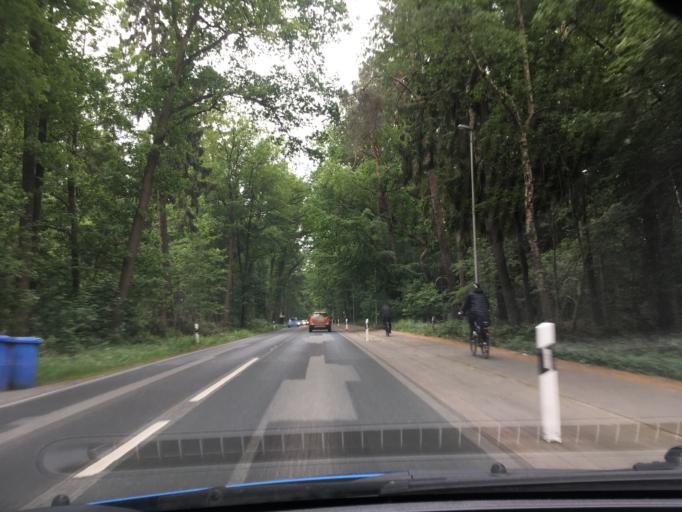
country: DE
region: Lower Saxony
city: Buchholz in der Nordheide
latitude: 53.3430
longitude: 9.8811
